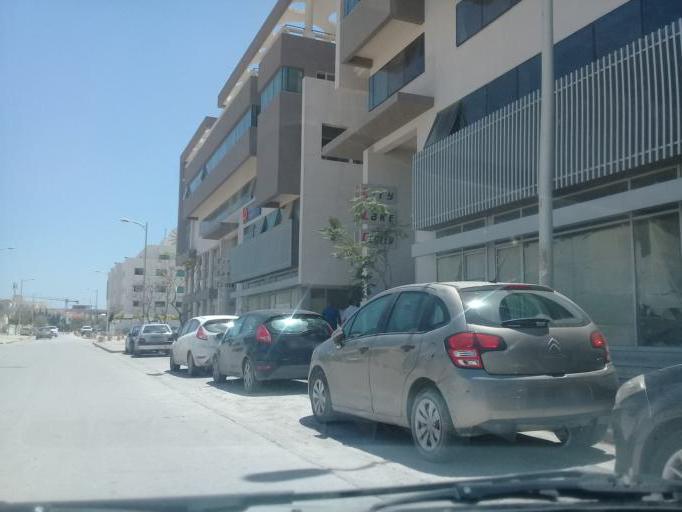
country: TN
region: Tunis
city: La Goulette
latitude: 36.8470
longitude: 10.2709
